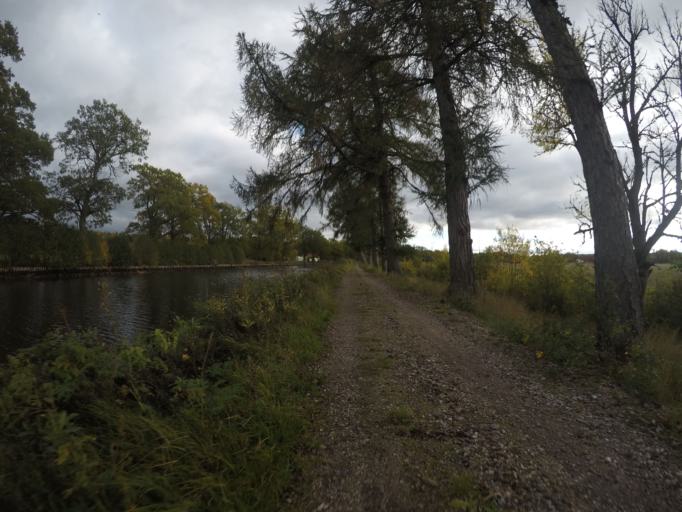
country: SE
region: Vaestmanland
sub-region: Arboga Kommun
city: Tyringe
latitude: 59.3910
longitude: 15.9379
